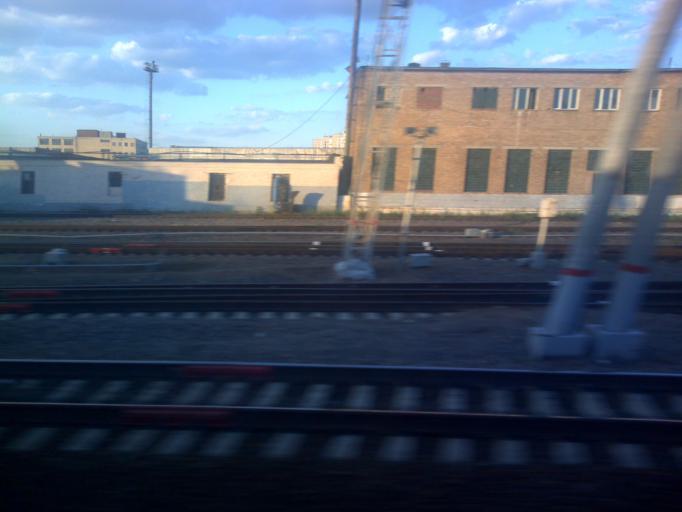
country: RU
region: Moscow
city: Lefortovo
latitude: 55.7428
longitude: 37.6943
